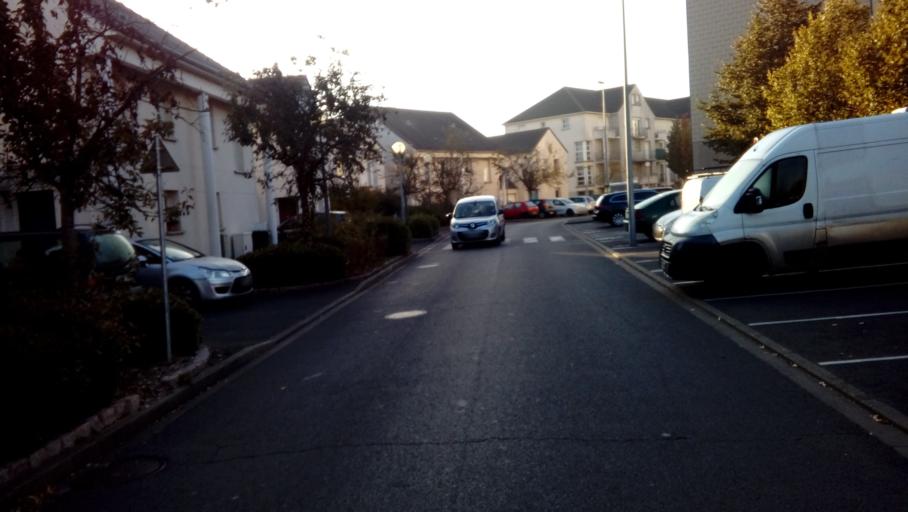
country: FR
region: Centre
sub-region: Departement du Loiret
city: Fleury-les-Aubrais
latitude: 47.9140
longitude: 1.9285
